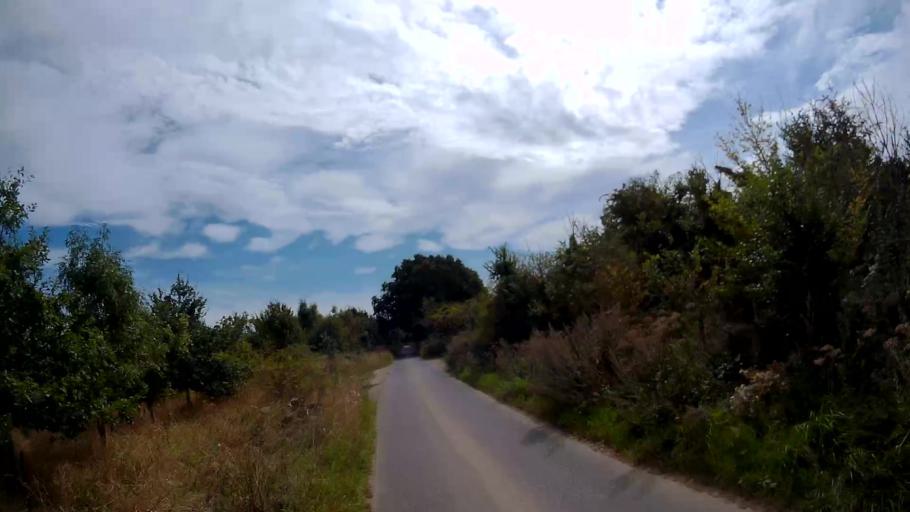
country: GB
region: England
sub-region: Hampshire
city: Odiham
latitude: 51.2325
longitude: -0.9628
